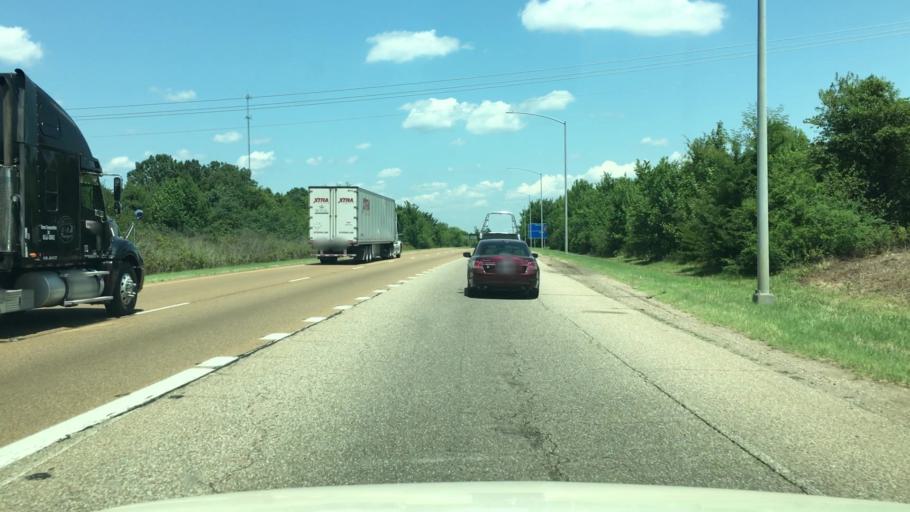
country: US
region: Arkansas
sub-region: Nevada County
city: Prescott
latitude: 33.8134
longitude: -93.4192
